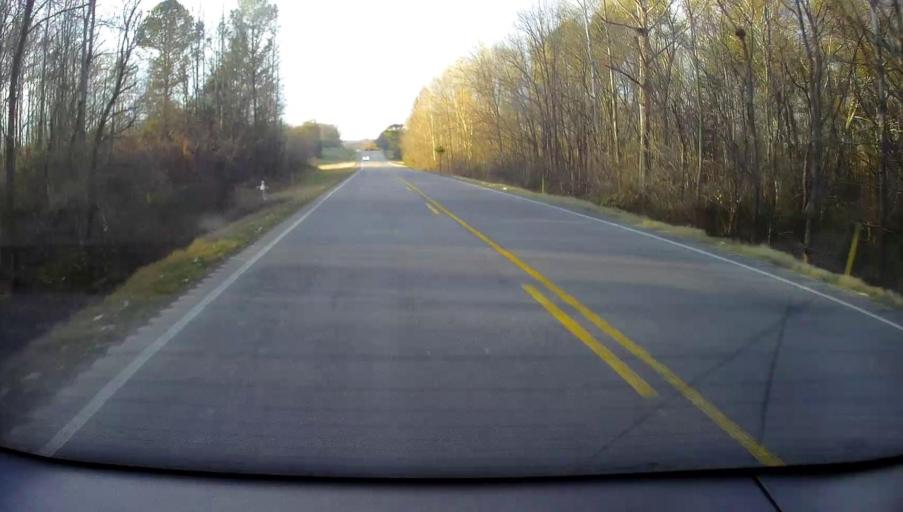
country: US
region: Alabama
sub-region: Blount County
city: Blountsville
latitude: 34.1574
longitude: -86.4639
